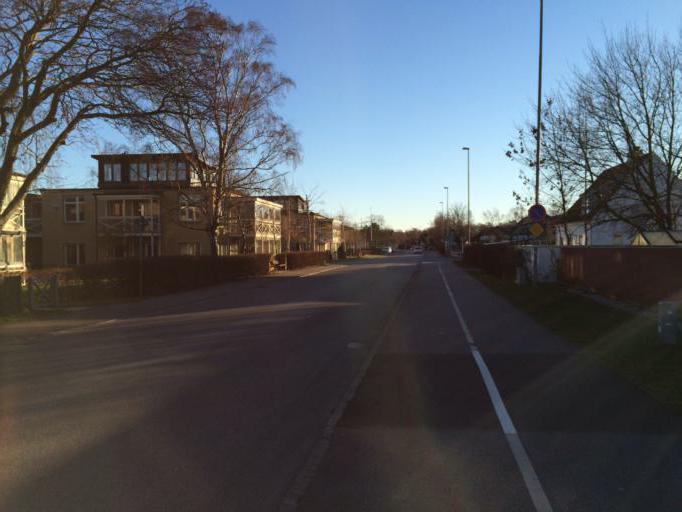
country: SE
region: Skane
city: Bjarred
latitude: 55.7192
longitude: 13.0286
